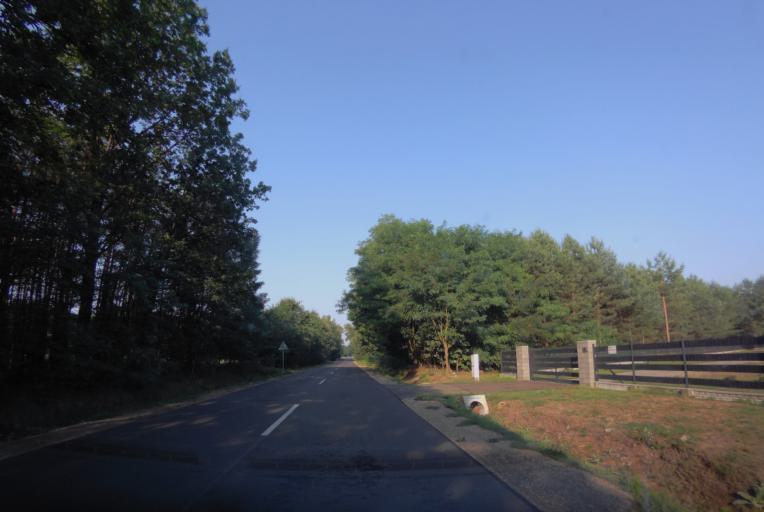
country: PL
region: Subcarpathian Voivodeship
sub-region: Powiat nizanski
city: Jarocin
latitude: 50.5100
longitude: 22.3207
